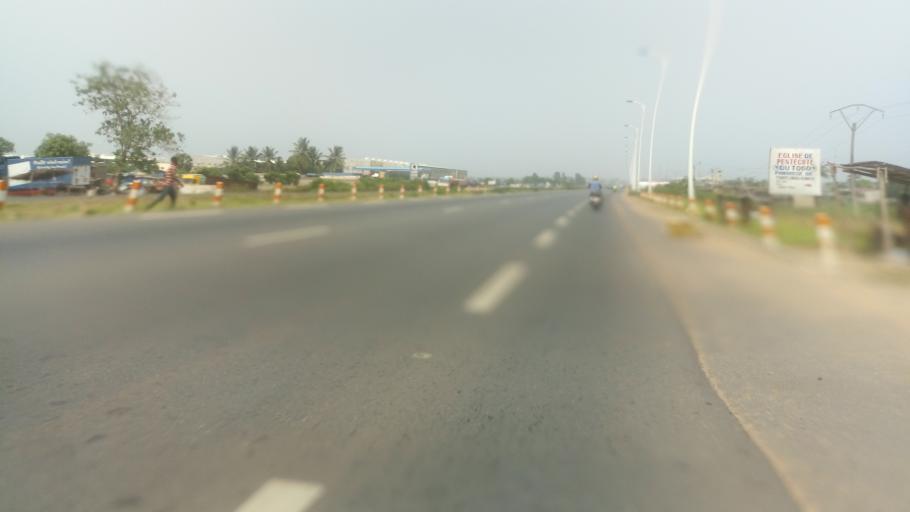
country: TG
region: Maritime
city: Tsevie
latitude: 6.2941
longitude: 1.2135
